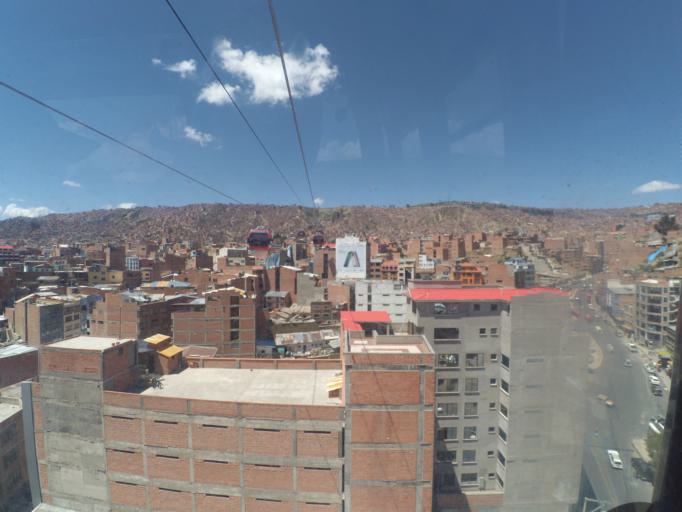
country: BO
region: La Paz
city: La Paz
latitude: -16.4934
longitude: -68.1471
